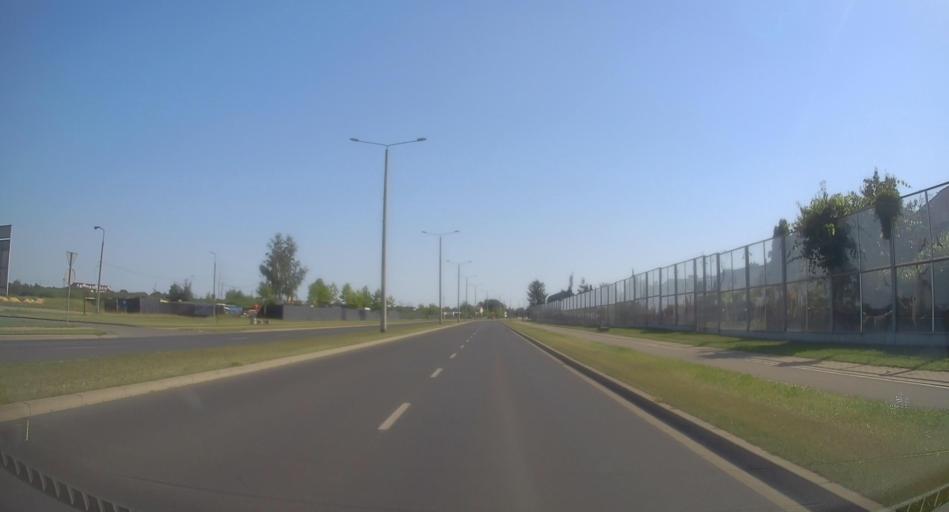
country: PL
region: Lodz Voivodeship
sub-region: Skierniewice
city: Skierniewice
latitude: 51.9523
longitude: 20.1589
